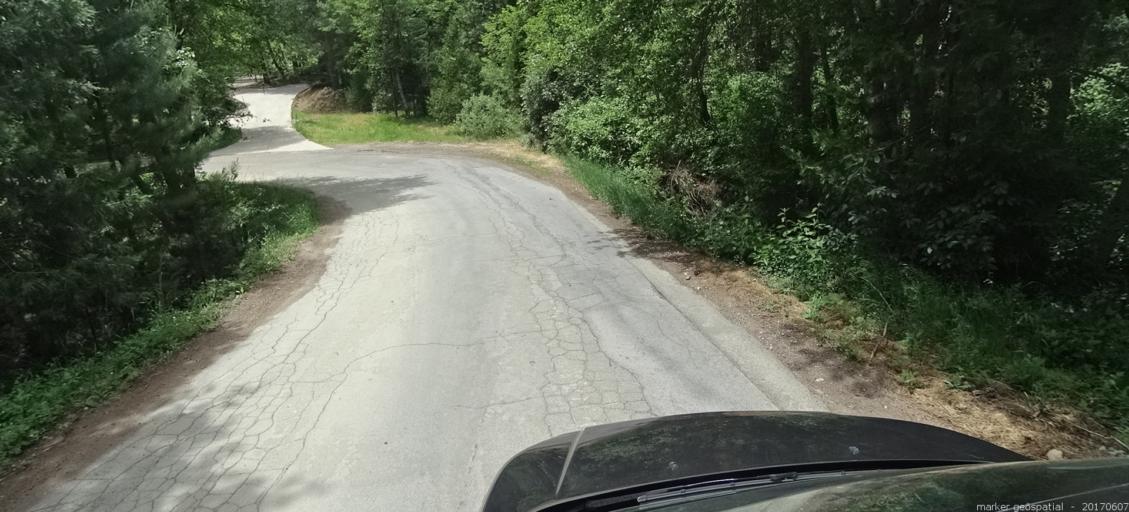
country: US
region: California
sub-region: Siskiyou County
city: Mount Shasta
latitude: 41.2939
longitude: -122.3285
